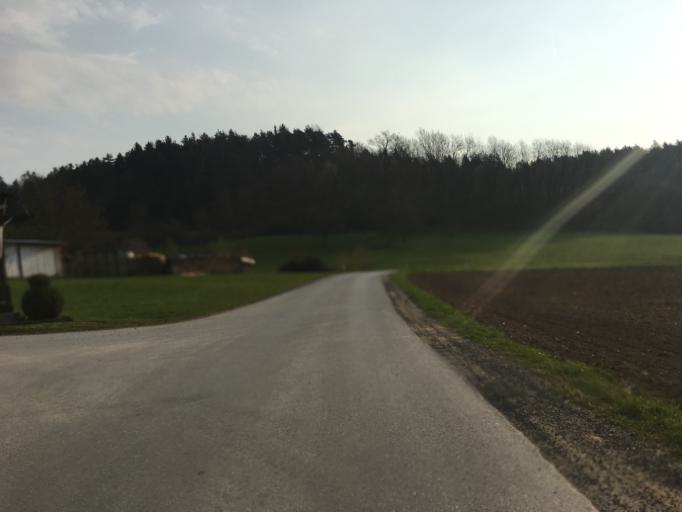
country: AT
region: Styria
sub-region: Politischer Bezirk Graz-Umgebung
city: Nestelbach bei Graz
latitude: 47.0835
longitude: 15.6237
